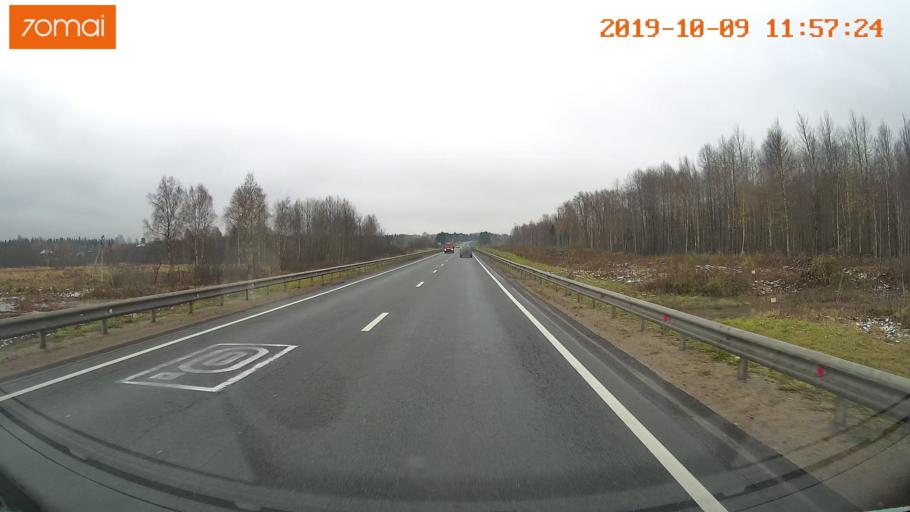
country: RU
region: Vologda
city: Gryazovets
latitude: 58.7327
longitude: 40.2924
